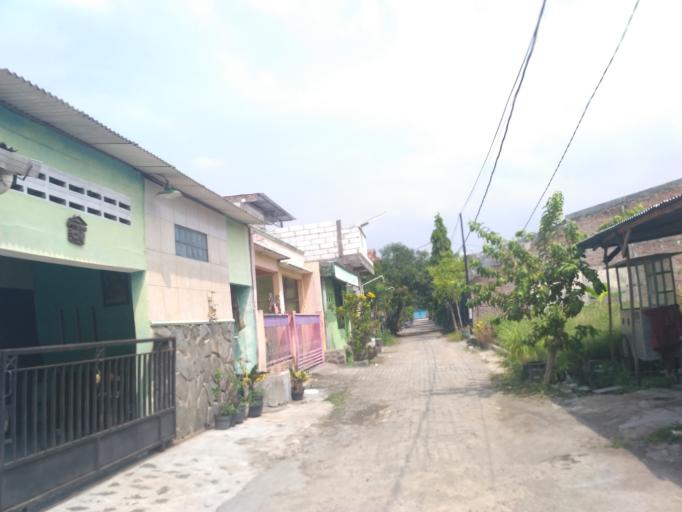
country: ID
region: Central Java
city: Mranggen
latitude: -7.0606
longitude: 110.4652
